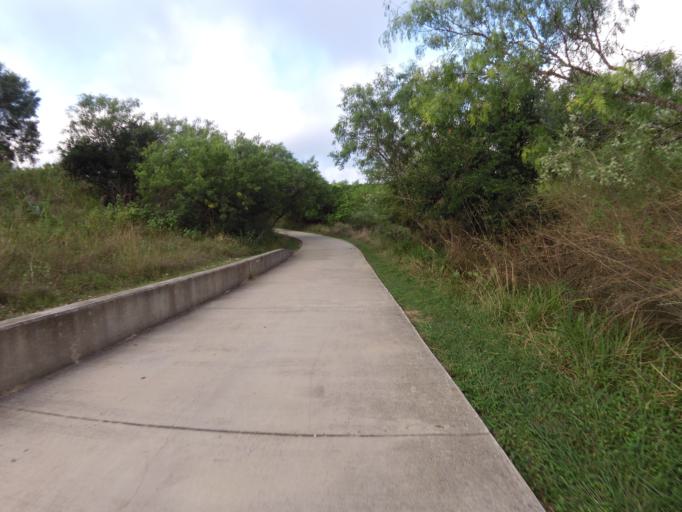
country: US
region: Texas
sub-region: Bexar County
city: Leon Valley
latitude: 29.5477
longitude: -98.6331
